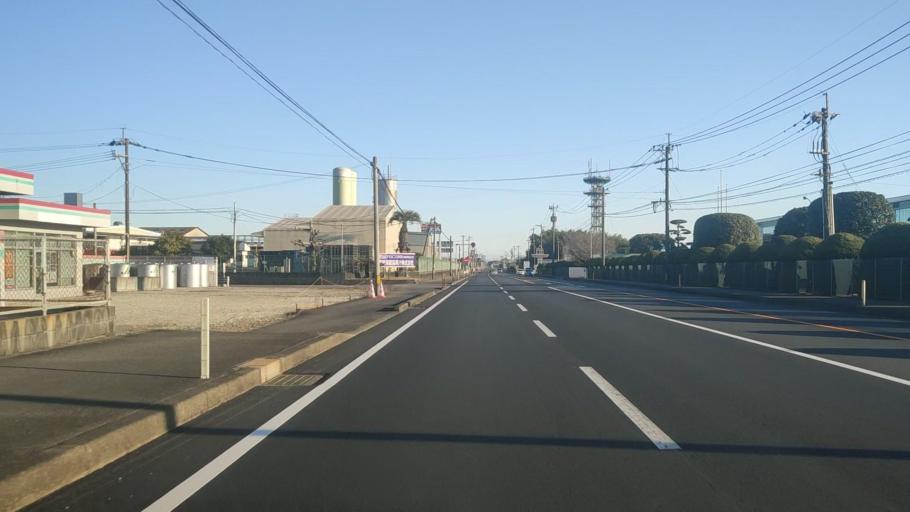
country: JP
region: Miyazaki
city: Takanabe
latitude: 32.2231
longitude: 131.5430
